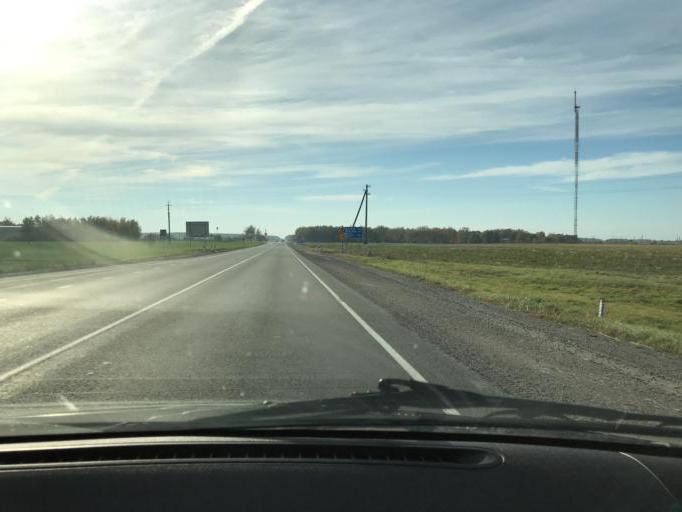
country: BY
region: Brest
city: Horad Pinsk
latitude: 52.1809
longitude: 26.0677
